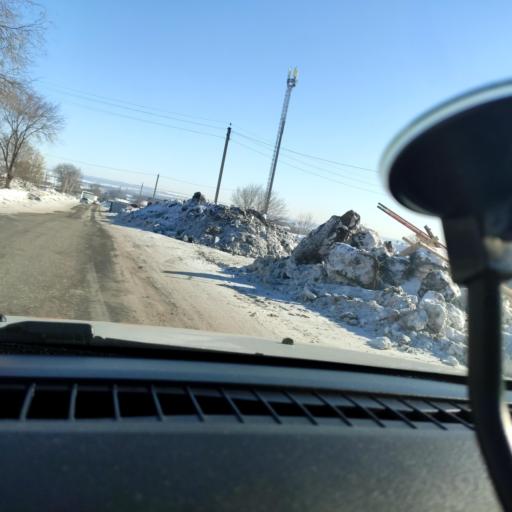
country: RU
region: Samara
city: Smyshlyayevka
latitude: 53.2565
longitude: 50.4896
